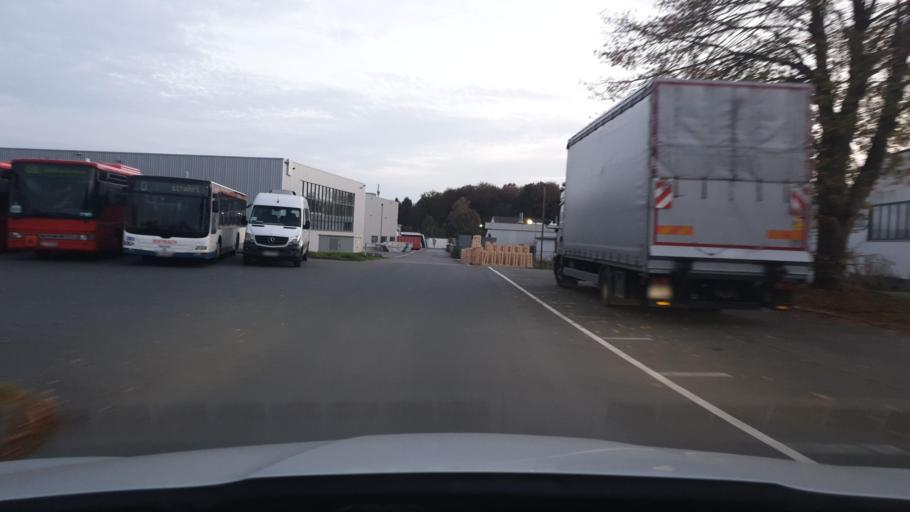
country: DE
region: North Rhine-Westphalia
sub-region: Regierungsbezirk Detmold
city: Bielefeld
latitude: 52.0689
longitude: 8.5819
